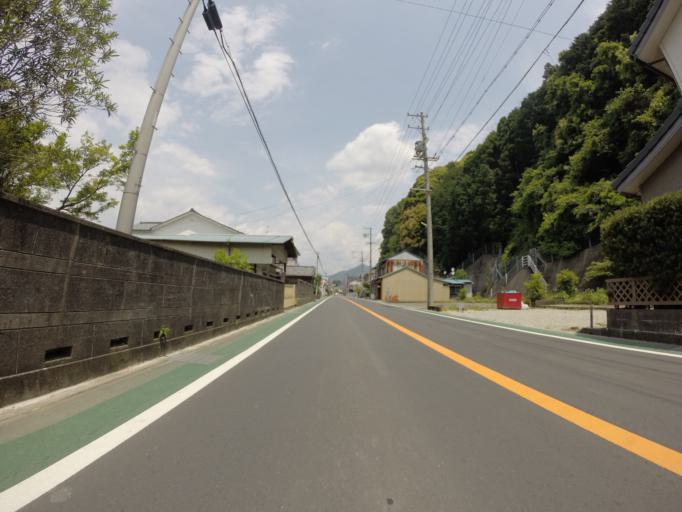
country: JP
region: Shizuoka
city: Shizuoka-shi
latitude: 35.0665
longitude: 138.3699
